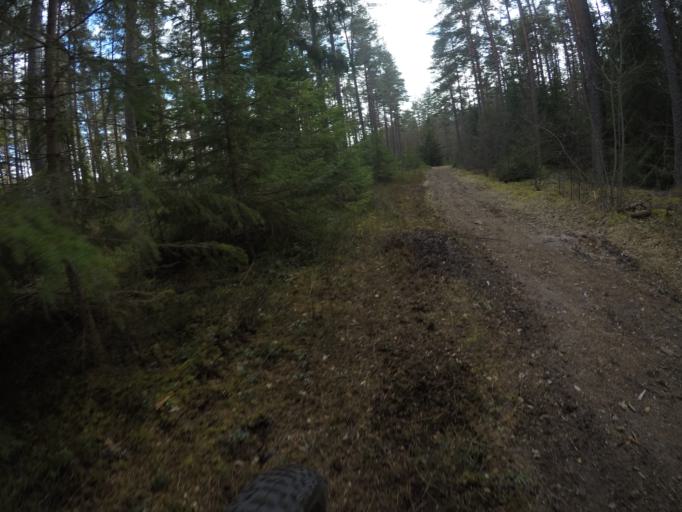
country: SE
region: Vaestmanland
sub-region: Kungsors Kommun
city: Kungsoer
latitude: 59.3503
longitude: 16.1072
